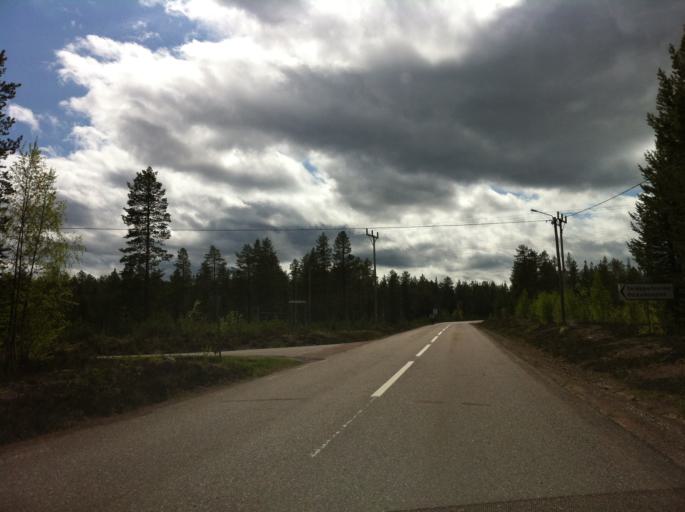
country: NO
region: Hedmark
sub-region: Trysil
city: Innbygda
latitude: 61.6835
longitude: 13.1276
